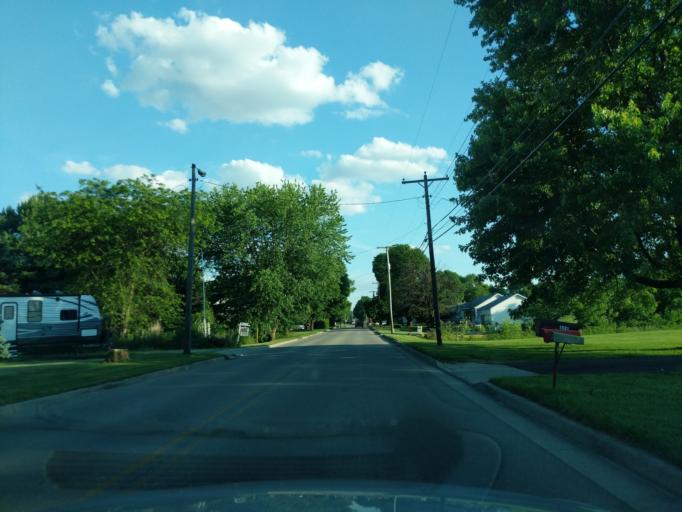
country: US
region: Indiana
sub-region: Huntington County
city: Huntington
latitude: 40.8774
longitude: -85.4710
